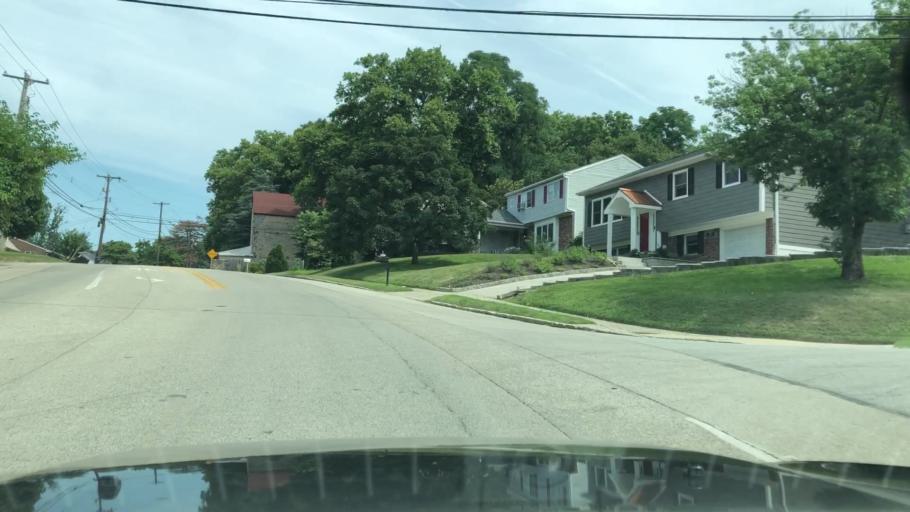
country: US
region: Pennsylvania
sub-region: Montgomery County
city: Norristown
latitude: 40.1157
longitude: -75.3070
